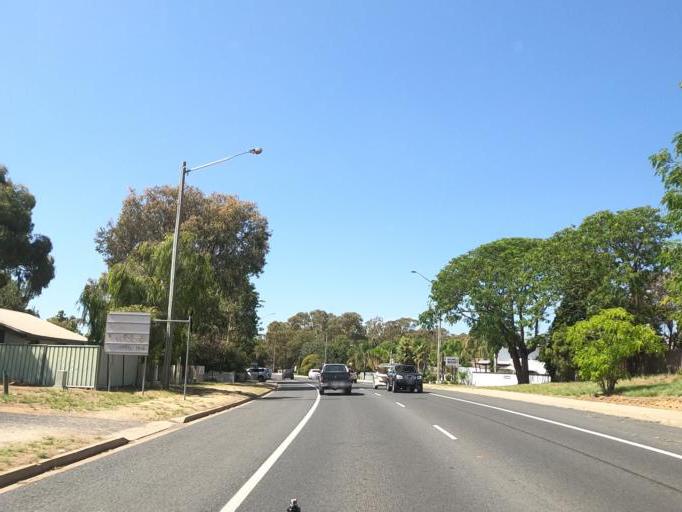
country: AU
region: New South Wales
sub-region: Corowa Shire
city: Mulwala
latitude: -35.9990
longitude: 146.0006
